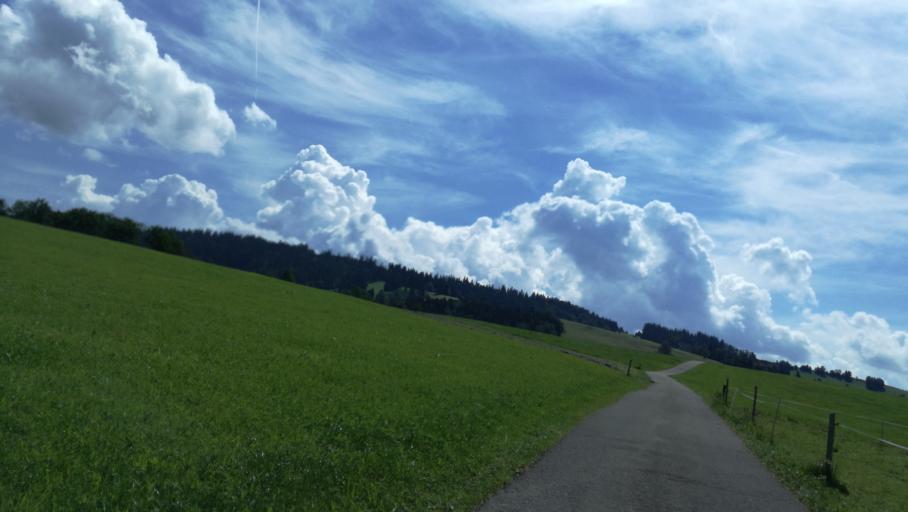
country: CH
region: Schwyz
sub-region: Bezirk Schwyz
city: Rothenthurm
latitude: 47.1376
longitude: 8.6425
